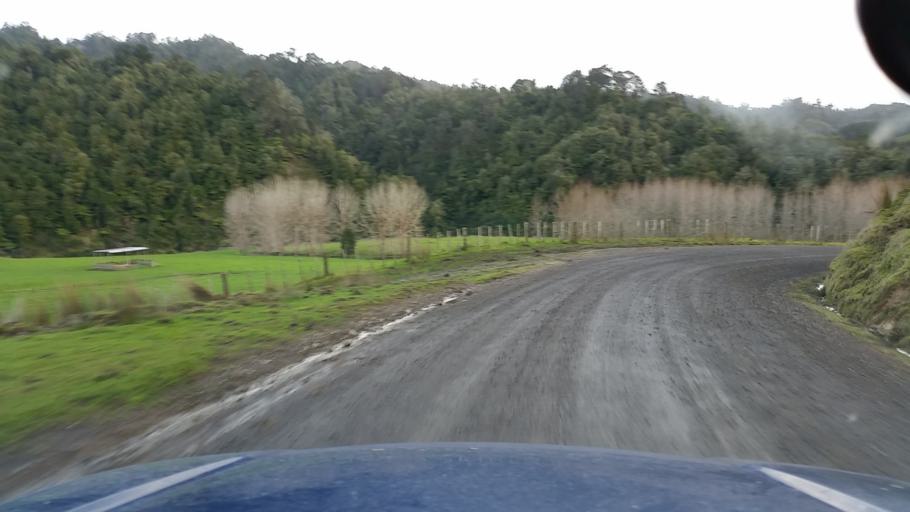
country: NZ
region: Taranaki
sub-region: South Taranaki District
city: Patea
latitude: -39.5630
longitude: 174.5622
